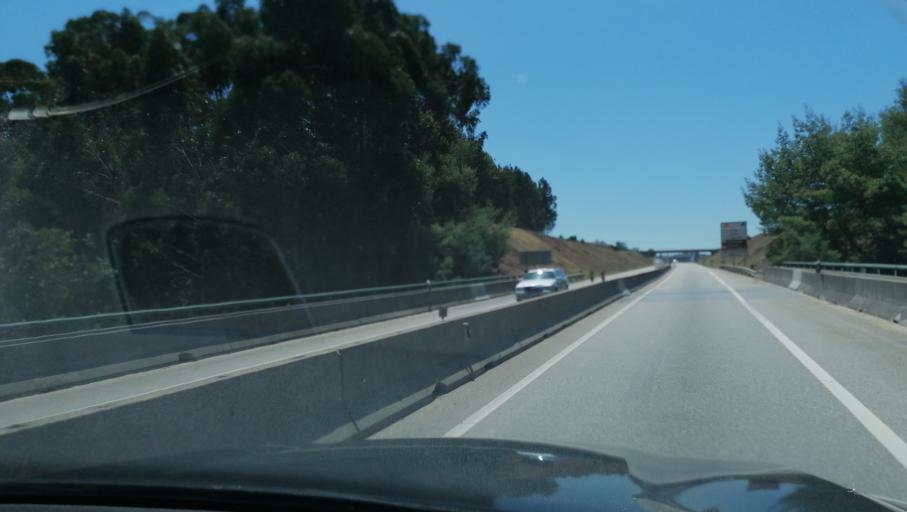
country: PT
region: Aveiro
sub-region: Agueda
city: Agueda
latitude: 40.5680
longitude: -8.4758
